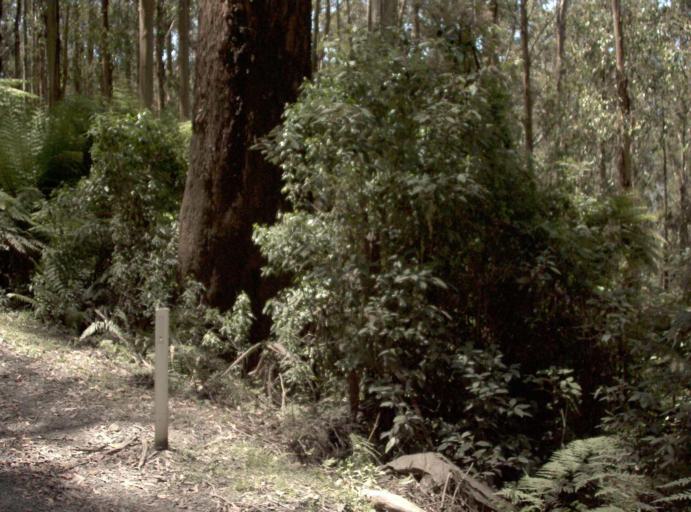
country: AU
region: Victoria
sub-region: Yarra Ranges
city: Millgrove
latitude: -37.7032
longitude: 145.7227
